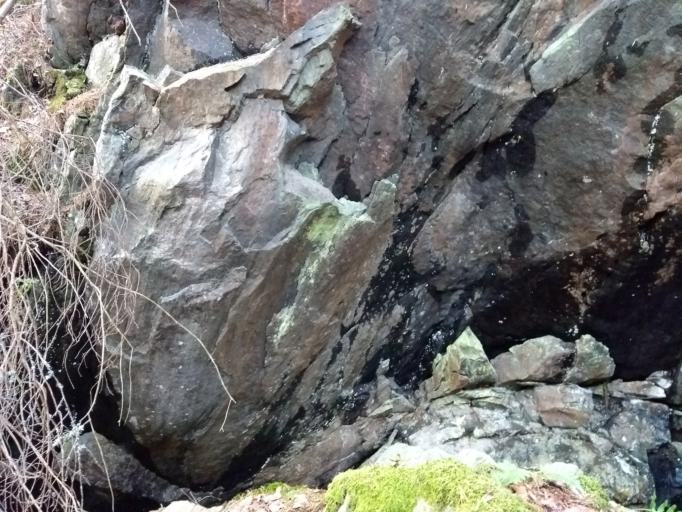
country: SE
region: OEstergoetland
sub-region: Norrkopings Kommun
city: Krokek
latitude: 58.6519
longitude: 16.4969
